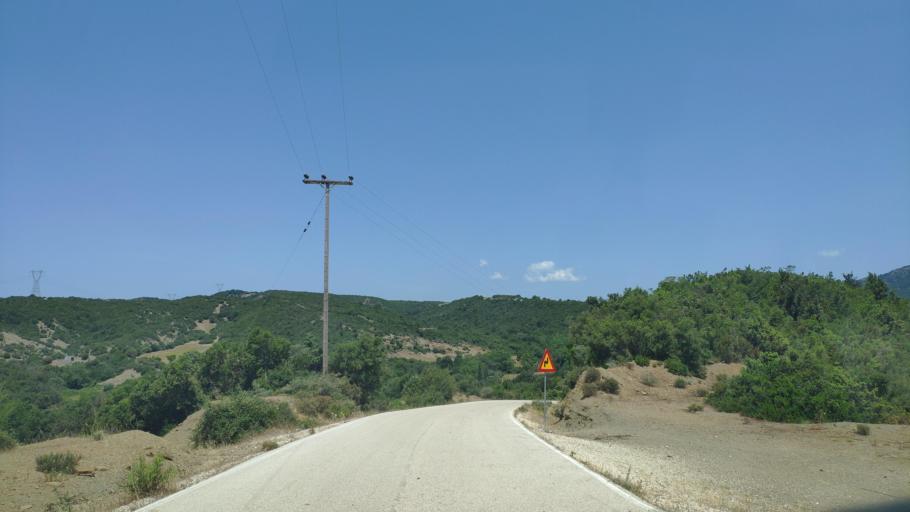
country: GR
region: West Greece
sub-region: Nomos Aitolias kai Akarnanias
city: Sardinia
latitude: 38.8732
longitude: 21.2802
